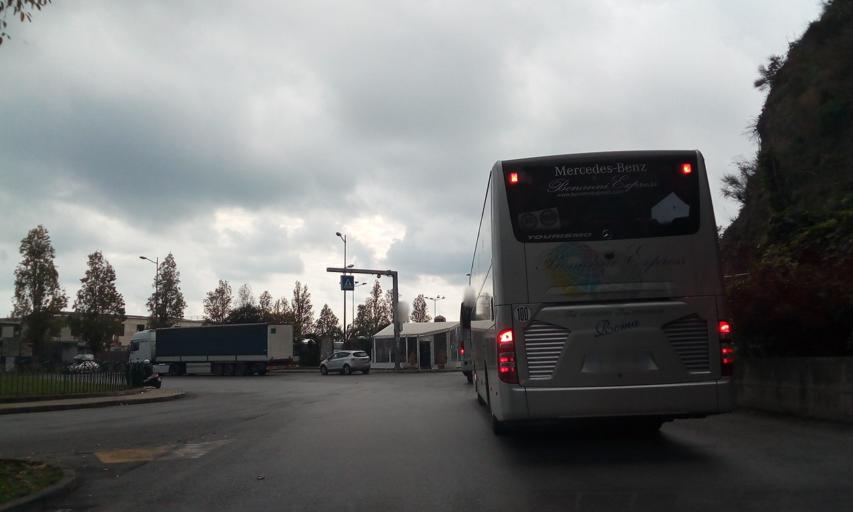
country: IT
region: Campania
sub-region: Provincia di Salerno
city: Vietri sul Mare
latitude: 40.6726
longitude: 14.7359
